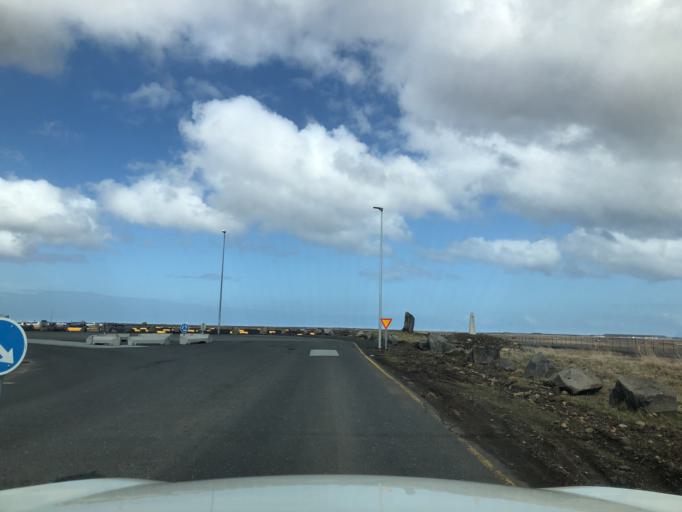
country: IS
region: Southern Peninsula
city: Reykjanesbaer
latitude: 63.9972
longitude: -22.6186
